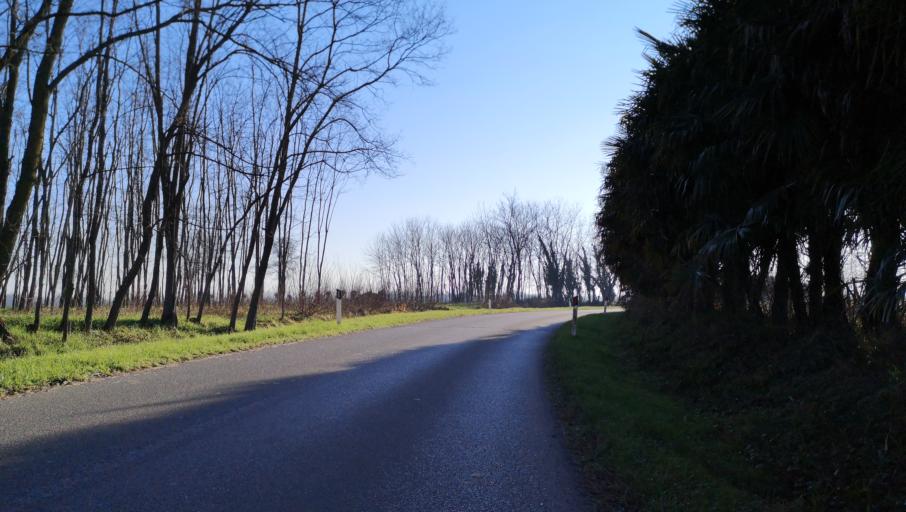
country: IT
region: Friuli Venezia Giulia
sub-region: Provincia di Udine
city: Santa Maria la Longa
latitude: 45.9514
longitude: 13.2701
